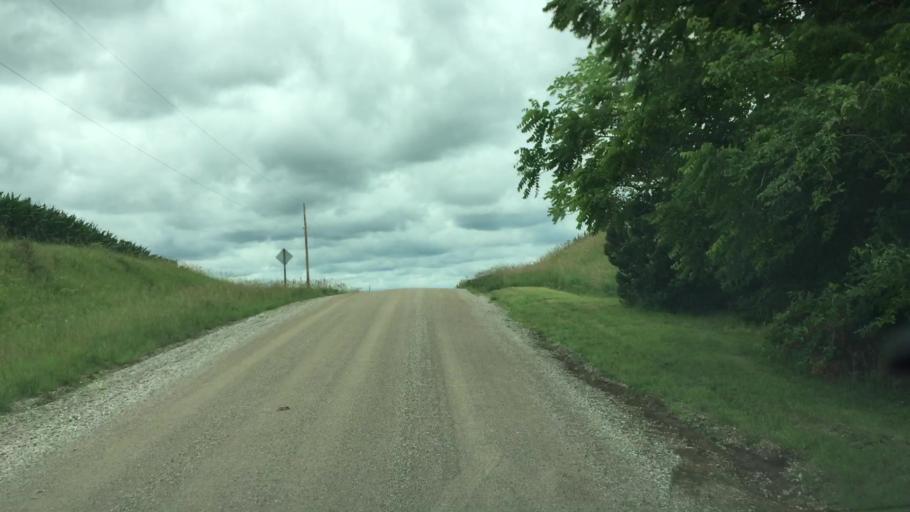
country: US
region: Iowa
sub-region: Jasper County
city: Monroe
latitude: 41.6010
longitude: -93.1188
